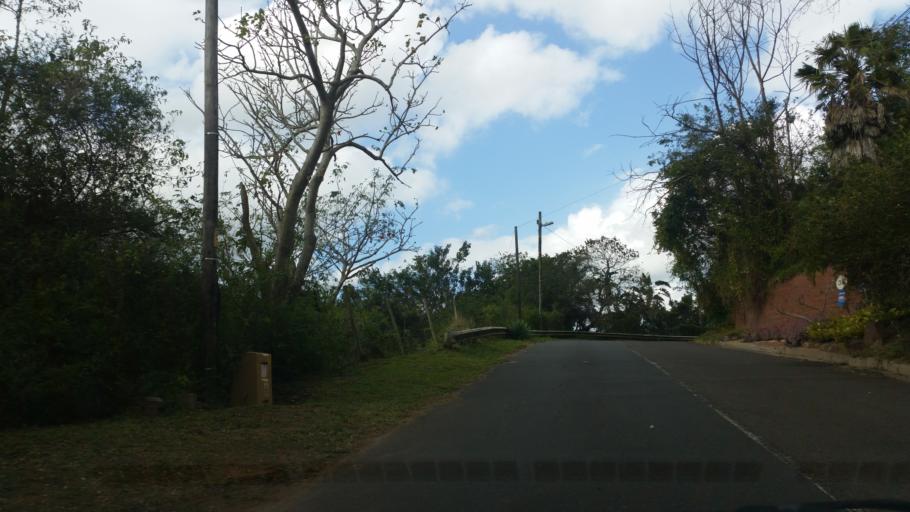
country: ZA
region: KwaZulu-Natal
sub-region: eThekwini Metropolitan Municipality
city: Berea
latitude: -29.8225
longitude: 30.9295
